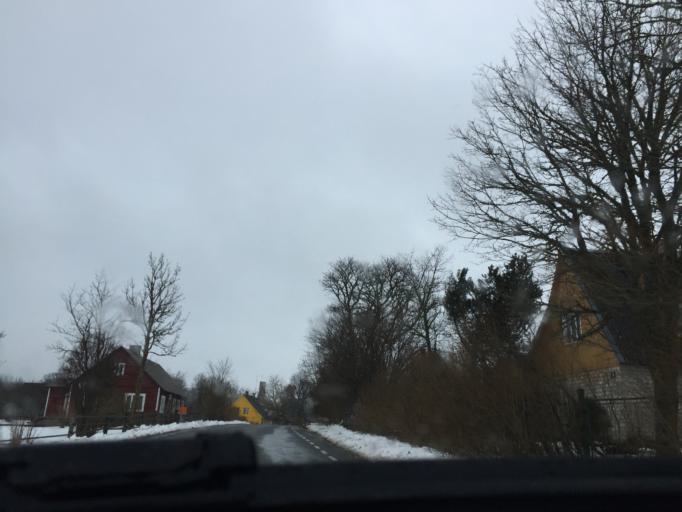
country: EE
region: Saare
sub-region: Kuressaare linn
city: Kuressaare
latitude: 58.3578
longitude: 22.0358
